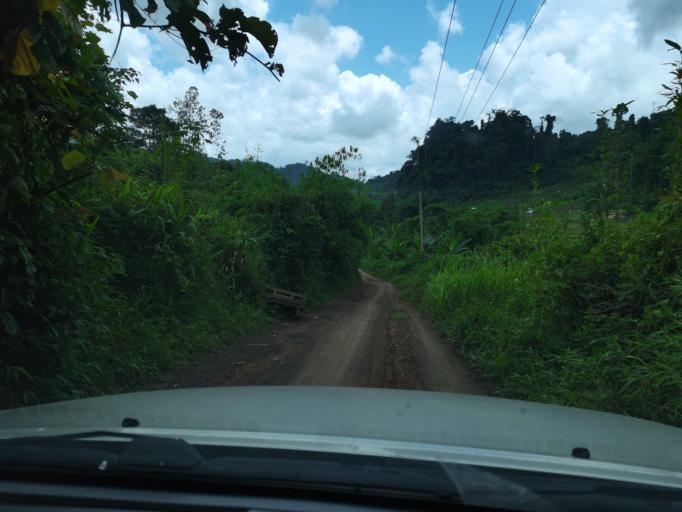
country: LA
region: Loungnamtha
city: Muang Long
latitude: 20.7596
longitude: 101.0168
